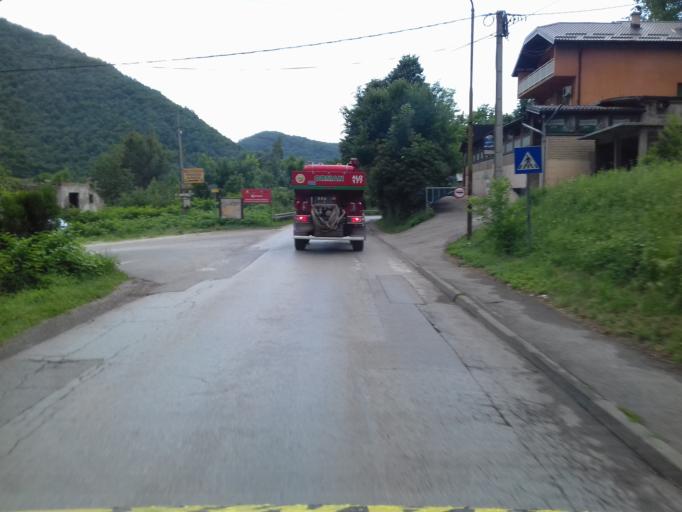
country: BA
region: Federation of Bosnia and Herzegovina
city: Visoko
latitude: 43.9720
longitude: 18.1878
